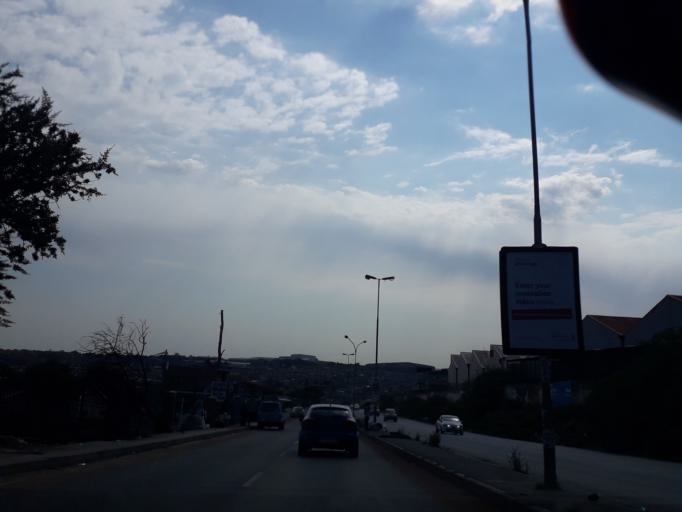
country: ZA
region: Gauteng
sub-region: City of Johannesburg Metropolitan Municipality
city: Modderfontein
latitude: -26.1125
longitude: 28.1040
